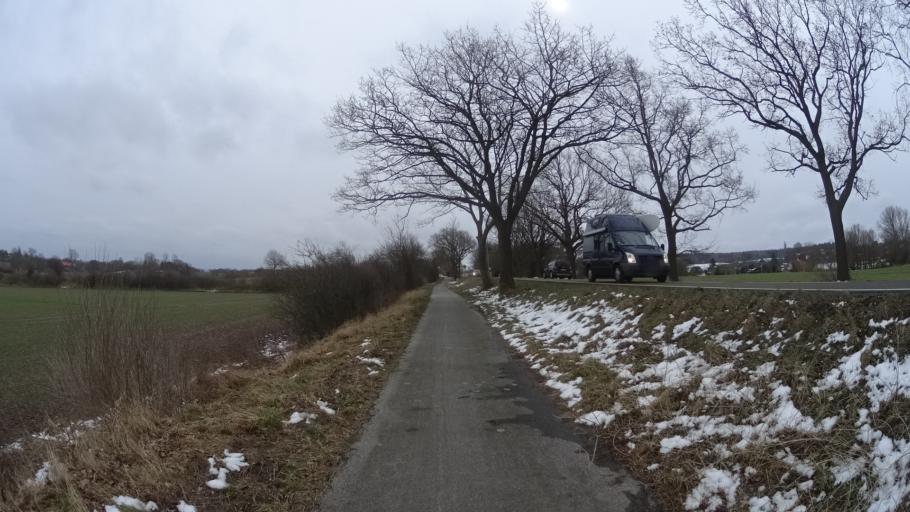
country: DE
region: Schleswig-Holstein
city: Panker
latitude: 54.3447
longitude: 10.5547
